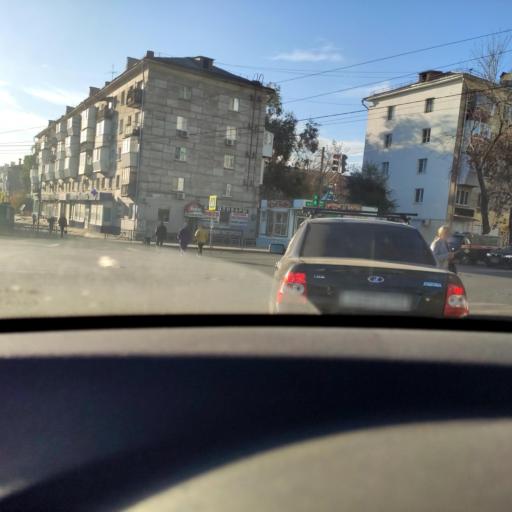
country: RU
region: Samara
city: Samara
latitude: 53.2094
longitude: 50.2312
